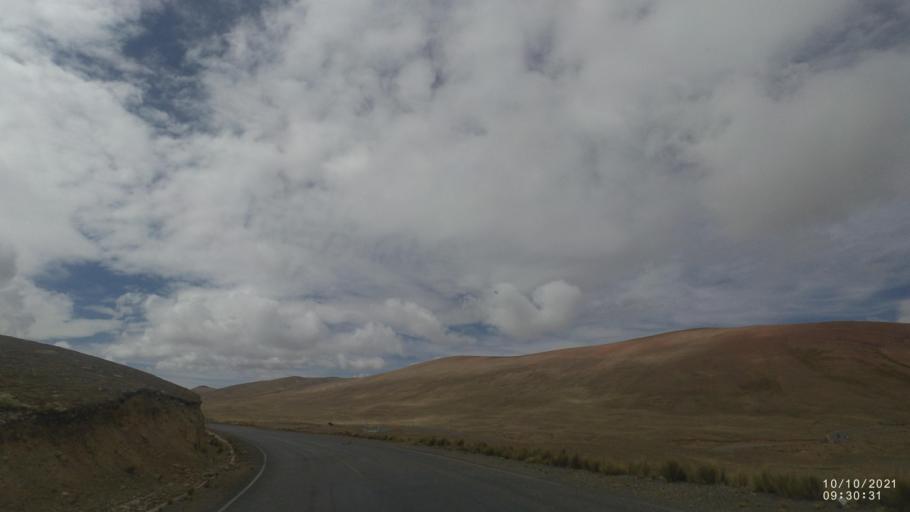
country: BO
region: La Paz
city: Quime
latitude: -17.1203
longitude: -67.3298
